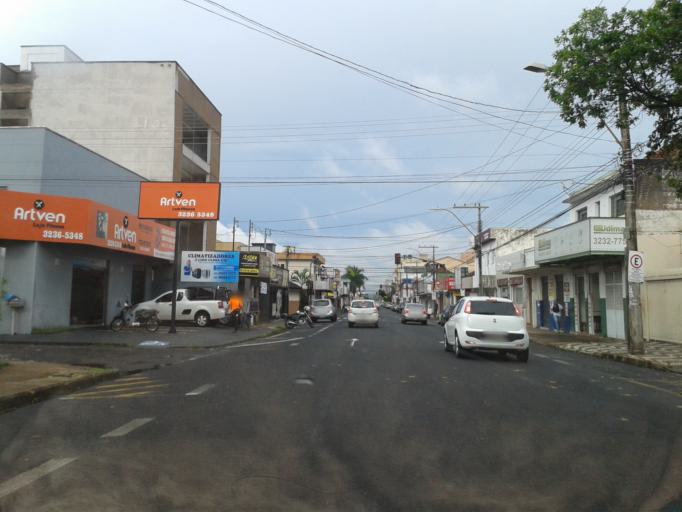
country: BR
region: Minas Gerais
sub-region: Uberlandia
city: Uberlandia
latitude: -18.9105
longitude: -48.2791
